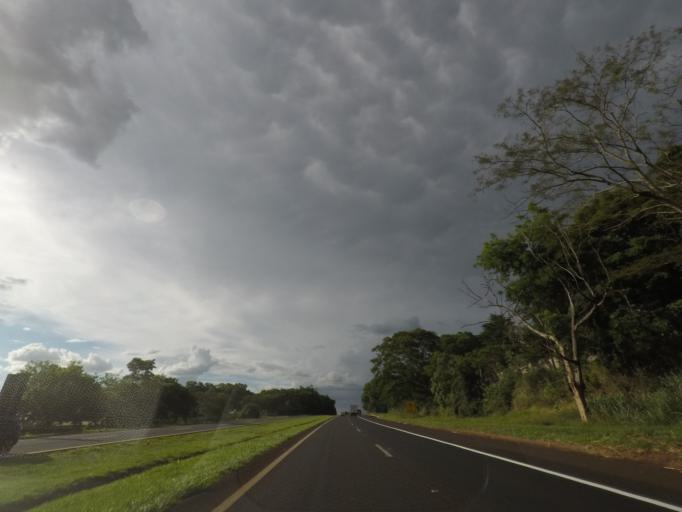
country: BR
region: Sao Paulo
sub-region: Jardinopolis
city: Jardinopolis
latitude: -21.0618
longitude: -47.8185
